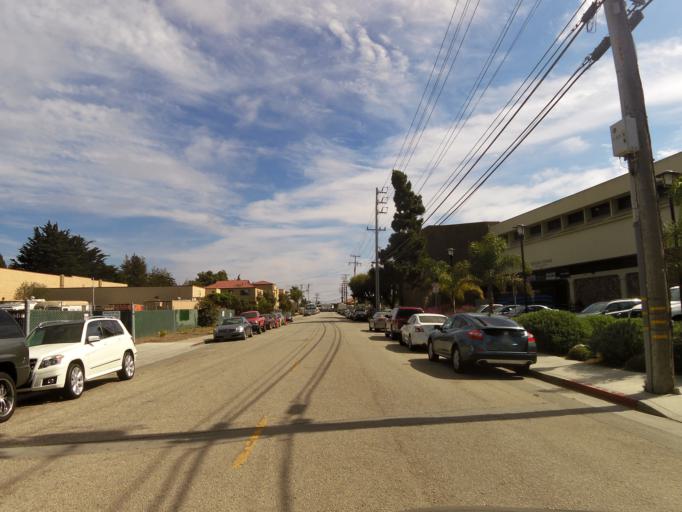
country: US
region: California
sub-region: Santa Cruz County
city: Santa Cruz
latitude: 36.9598
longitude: -122.0552
